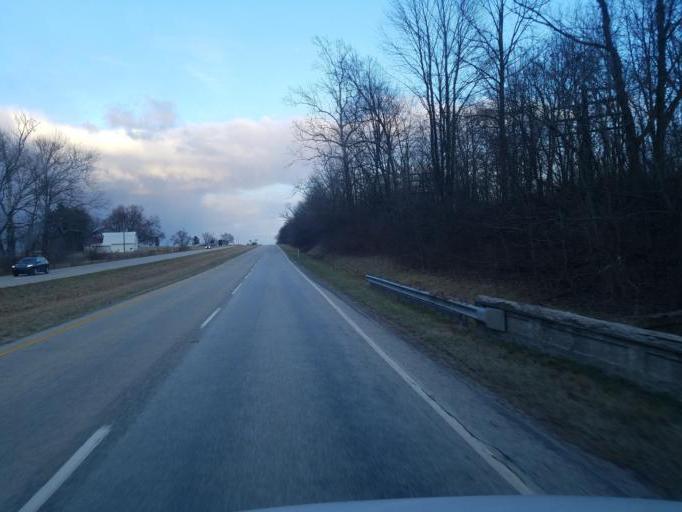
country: US
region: Indiana
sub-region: Henry County
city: Knightstown
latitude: 39.8021
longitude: -85.4739
